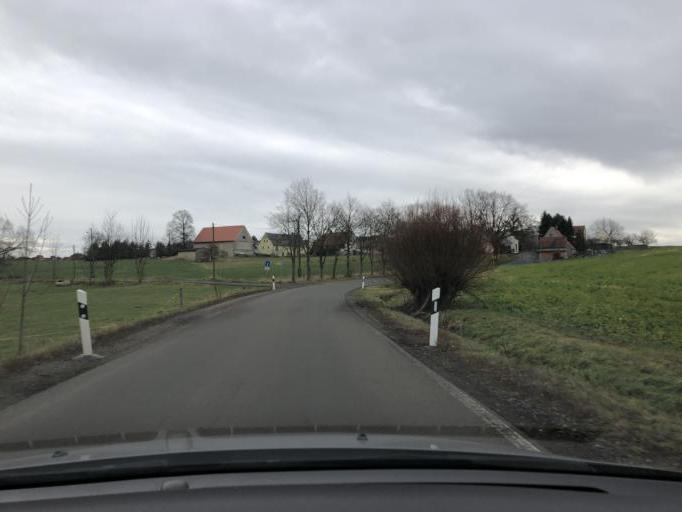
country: DE
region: Saxony
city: Nossen
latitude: 51.0762
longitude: 13.2944
